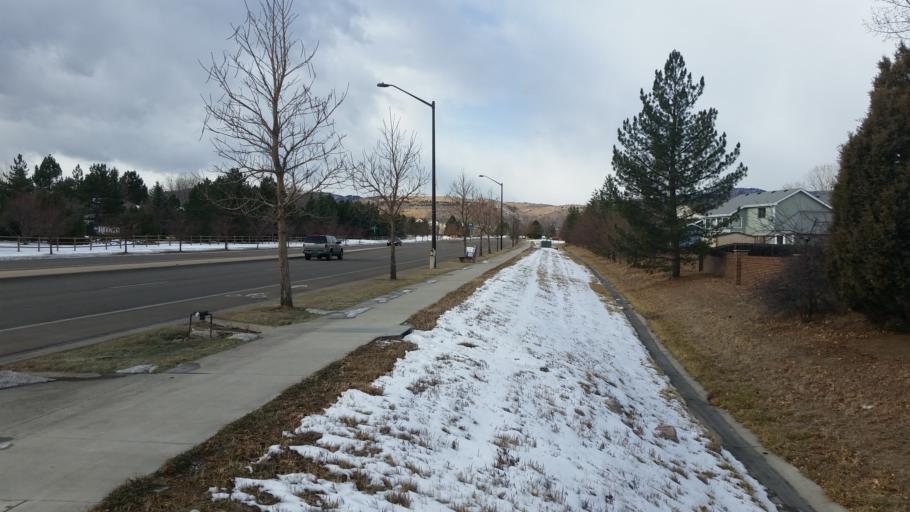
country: US
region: Colorado
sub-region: Larimer County
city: Fort Collins
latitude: 40.5238
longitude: -105.1028
